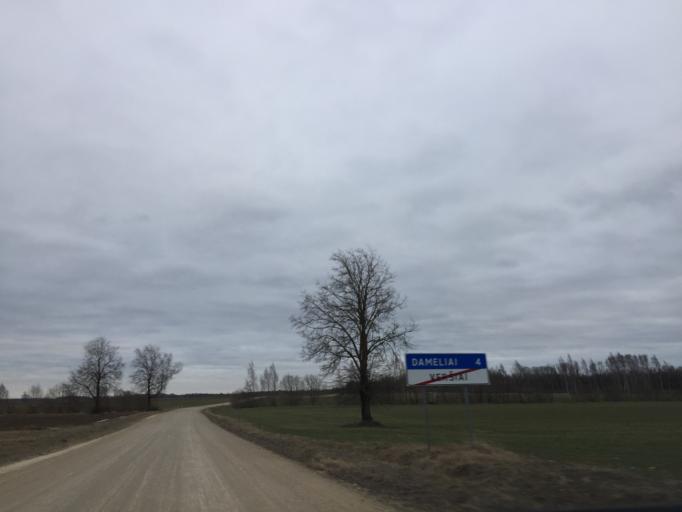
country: LT
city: Zagare
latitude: 56.3124
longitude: 23.2506
